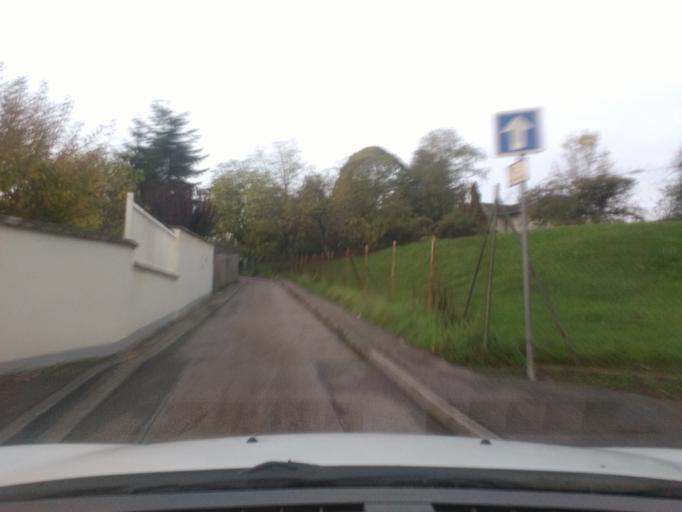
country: FR
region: Lorraine
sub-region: Departement des Vosges
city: Mirecourt
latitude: 48.3045
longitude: 6.1299
